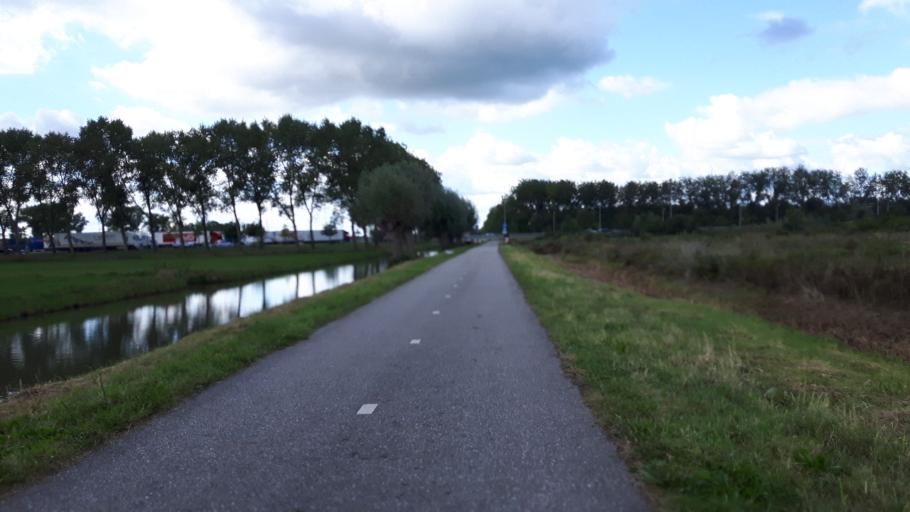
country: NL
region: Gelderland
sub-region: Gemeente Culemborg
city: Culemborg
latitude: 51.9143
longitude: 5.1822
